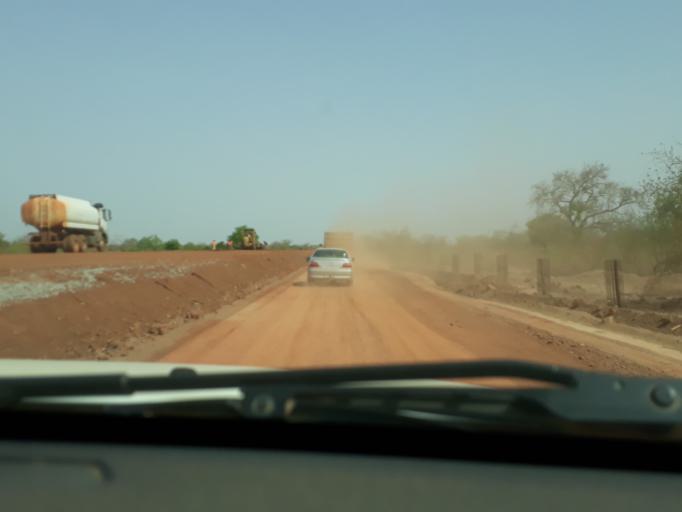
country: BF
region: Centre
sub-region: Kadiogo Province
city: Ouagadougou
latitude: 12.5841
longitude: -1.5245
